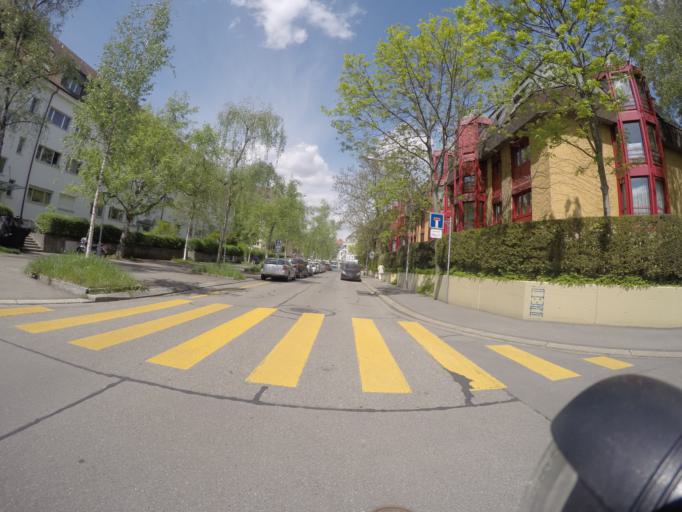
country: CH
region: Zurich
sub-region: Bezirk Zuerich
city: Zuerich (Kreis 6)
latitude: 47.3947
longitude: 8.5411
